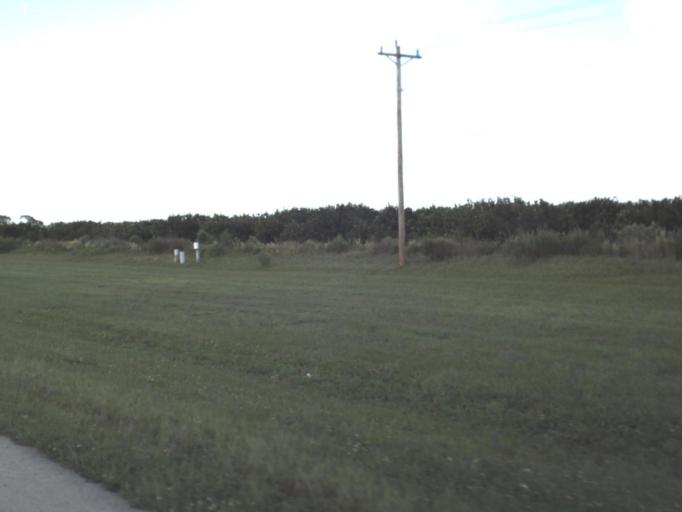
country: US
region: Florida
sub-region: Collier County
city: Immokalee
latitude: 26.4965
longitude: -81.4775
